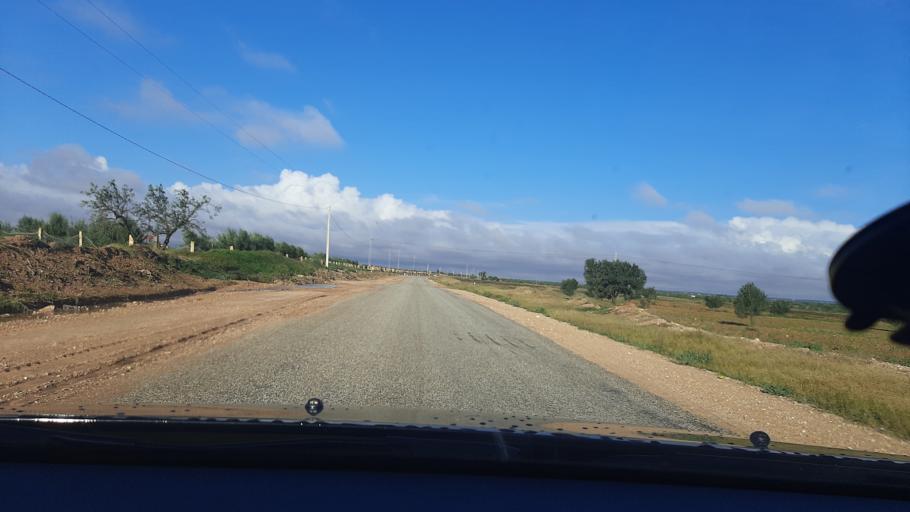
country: TN
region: Safaqis
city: Sfax
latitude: 34.8872
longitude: 10.6250
